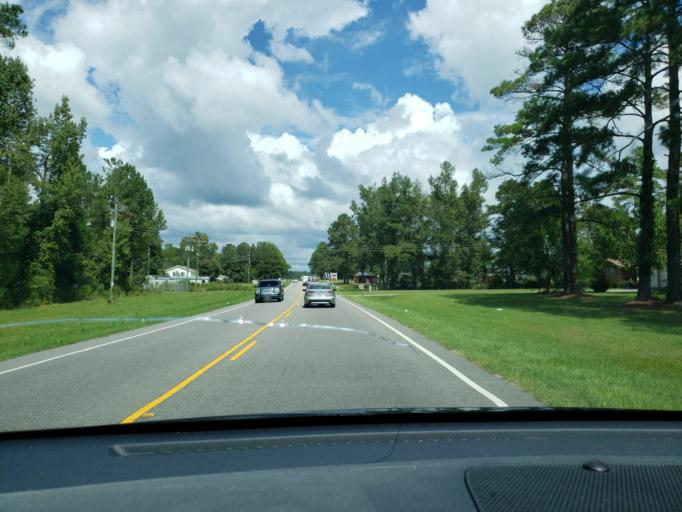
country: US
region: North Carolina
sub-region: Columbus County
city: Brunswick
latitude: 34.2679
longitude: -78.7419
